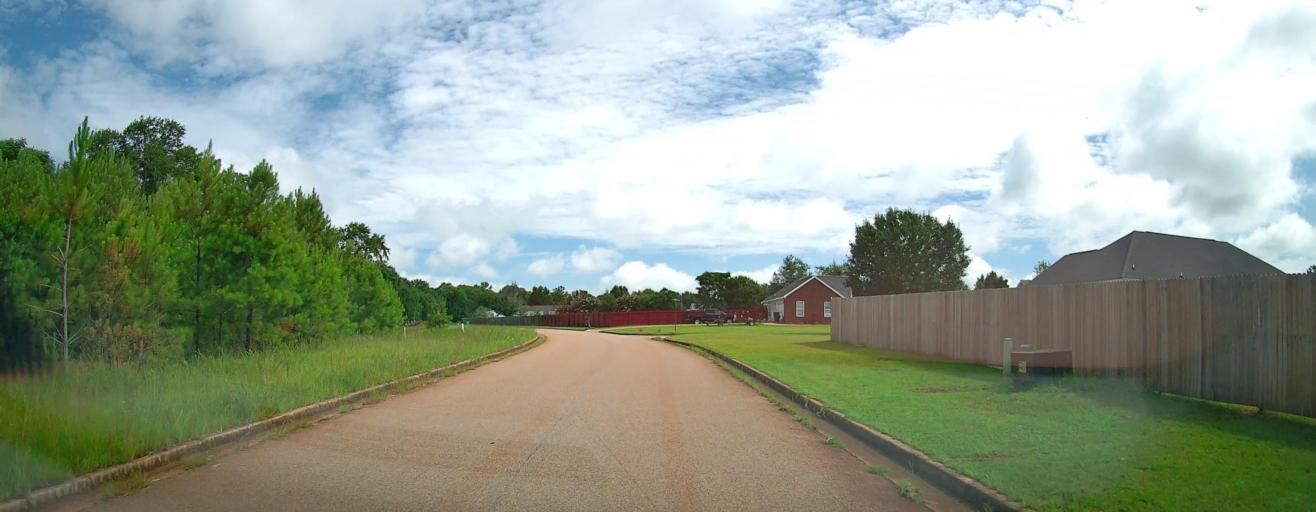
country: US
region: Georgia
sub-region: Houston County
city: Centerville
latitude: 32.6464
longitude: -83.7225
